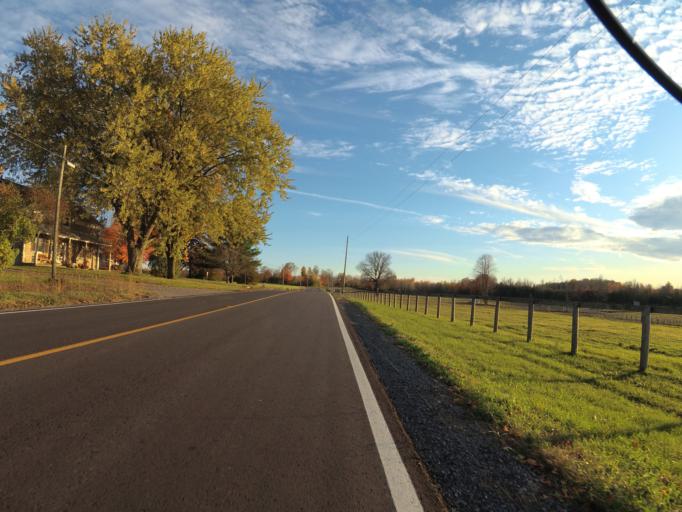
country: CA
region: Ontario
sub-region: Lanark County
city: Smiths Falls
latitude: 44.9537
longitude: -75.8143
